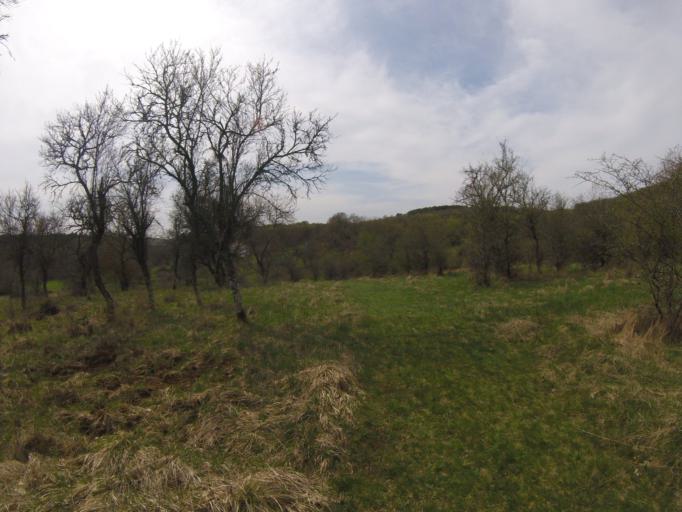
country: SK
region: Kosicky
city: Roznava
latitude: 48.5433
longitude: 20.6411
